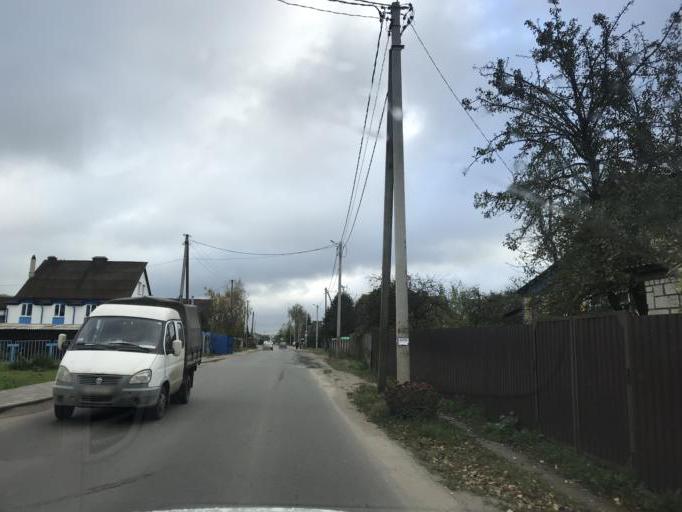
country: BY
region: Mogilev
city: Mahilyow
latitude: 53.8843
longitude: 30.3420
